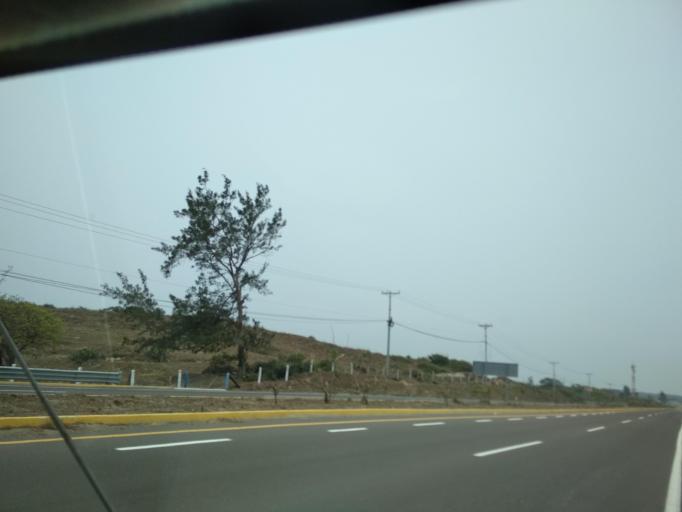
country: MX
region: Veracruz
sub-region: Alvarado
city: Playa de la Libertad
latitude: 19.0555
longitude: -96.0492
